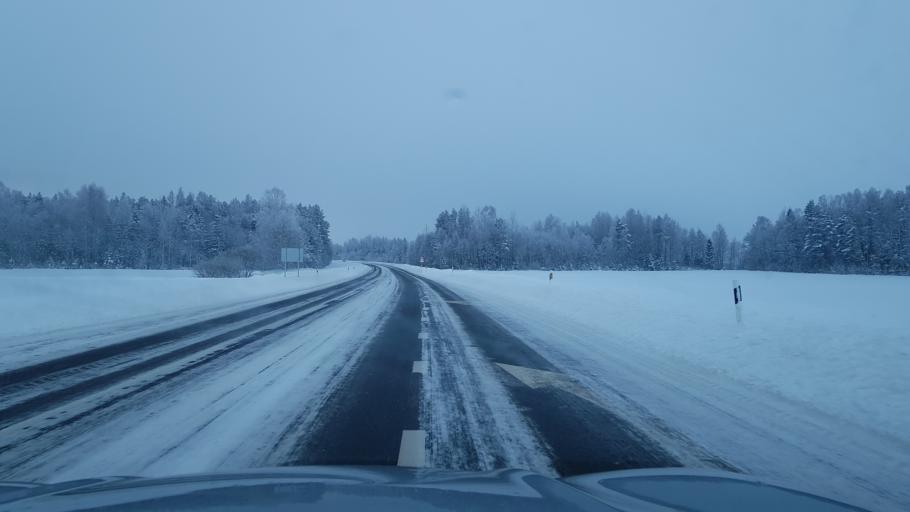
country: EE
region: Ida-Virumaa
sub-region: Johvi vald
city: Johvi
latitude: 59.2251
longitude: 27.3377
